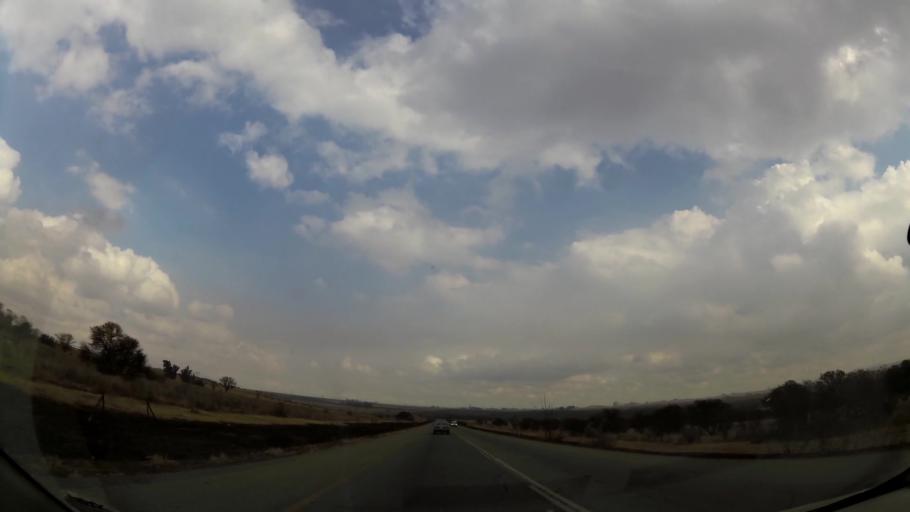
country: ZA
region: Orange Free State
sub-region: Fezile Dabi District Municipality
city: Sasolburg
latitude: -26.7952
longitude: 27.9162
